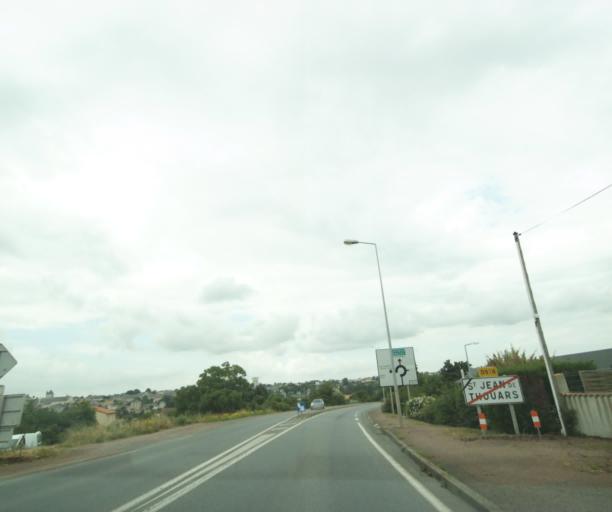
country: FR
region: Poitou-Charentes
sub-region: Departement des Deux-Sevres
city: Saint-Jean-de-Thouars
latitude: 46.9675
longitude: -0.2105
